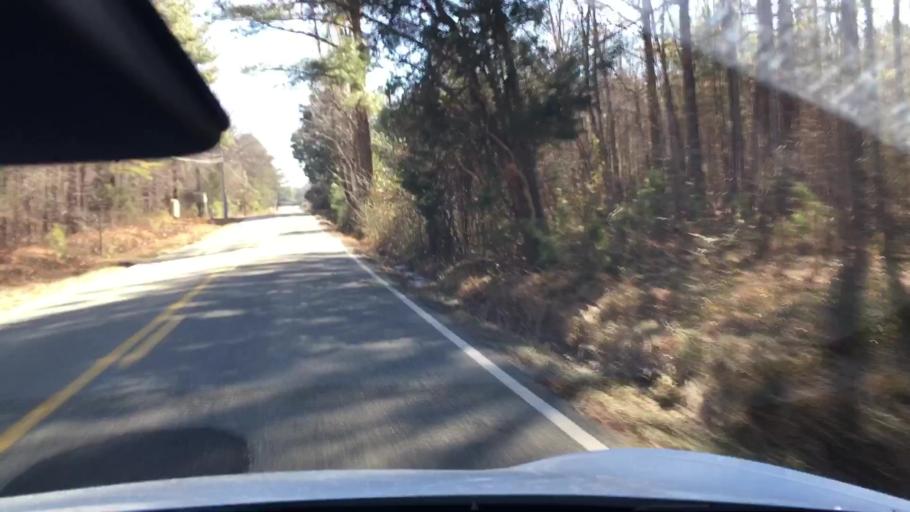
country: US
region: Virginia
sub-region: Henrico County
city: Short Pump
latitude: 37.5715
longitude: -77.7163
